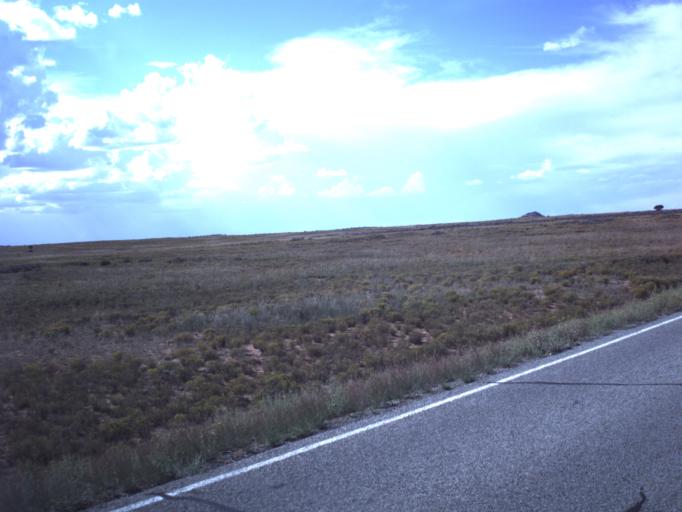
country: US
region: Utah
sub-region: Grand County
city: Moab
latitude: 38.5316
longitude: -109.7517
